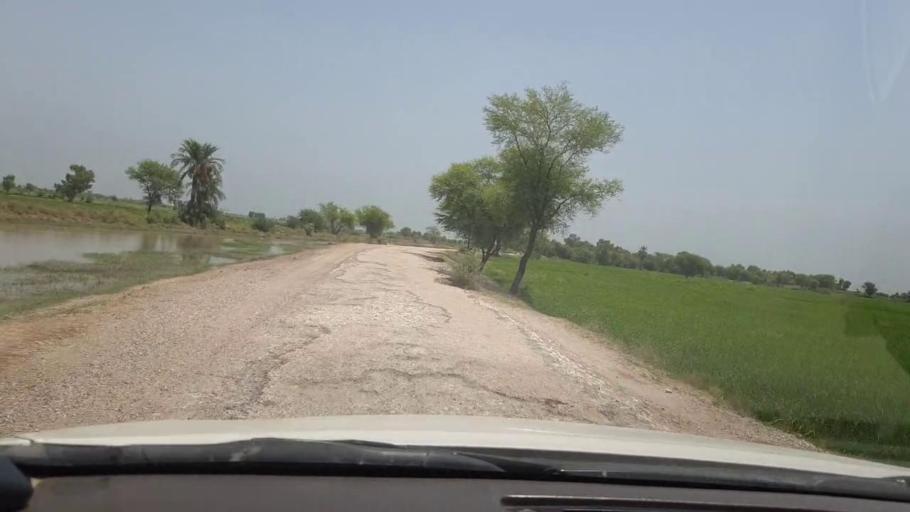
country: PK
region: Sindh
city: Garhi Yasin
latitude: 27.8957
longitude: 68.5340
